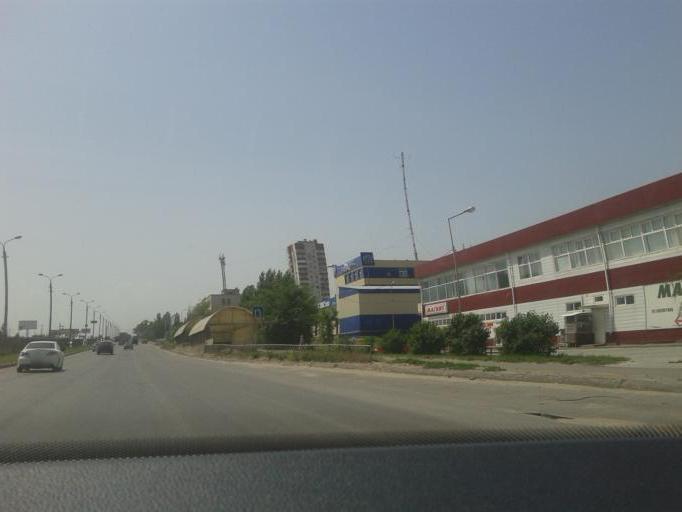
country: RU
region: Volgograd
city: Volgograd
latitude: 48.7574
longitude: 44.4934
